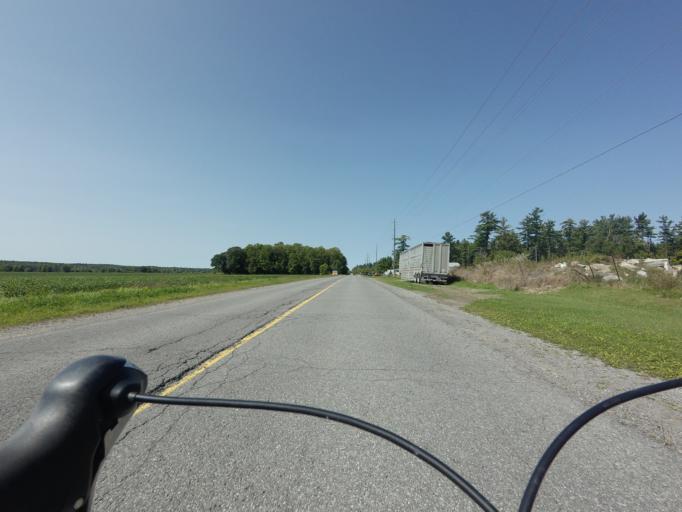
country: CA
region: Ontario
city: Arnprior
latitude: 45.4902
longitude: -76.1360
